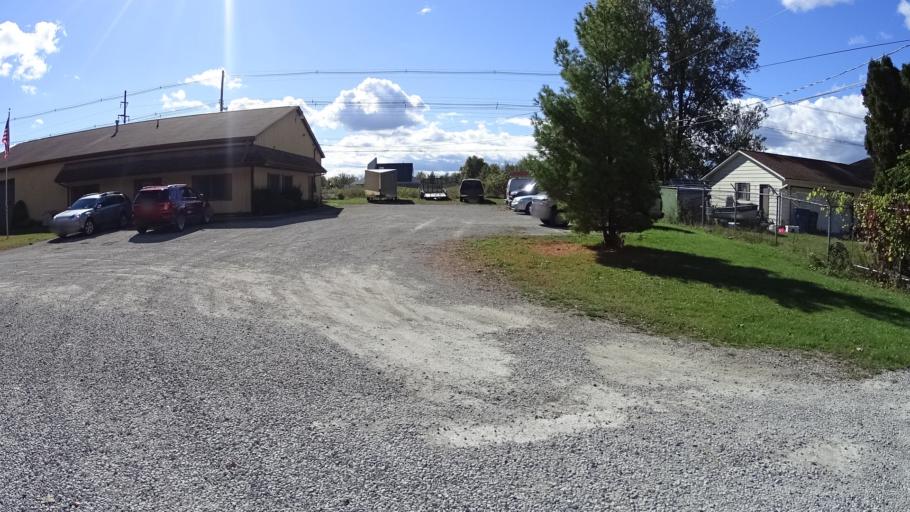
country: US
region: Ohio
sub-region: Lorain County
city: Grafton
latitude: 41.2808
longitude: -82.0603
